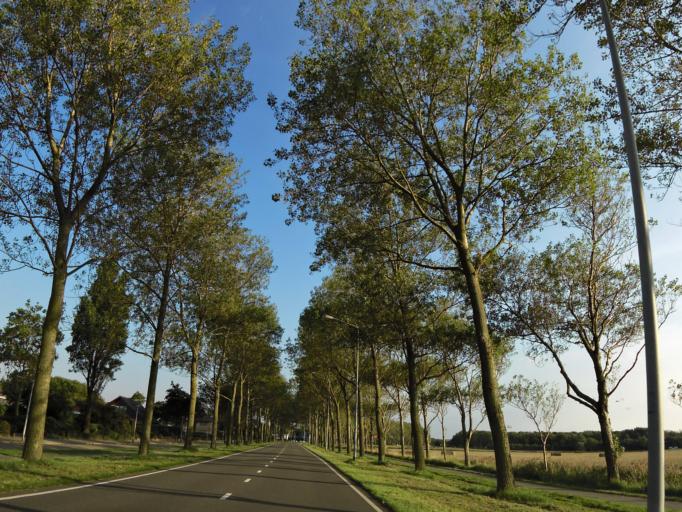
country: NL
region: Zeeland
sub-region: Gemeente Vlissingen
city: Vlissingen
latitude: 51.4626
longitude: 3.5410
